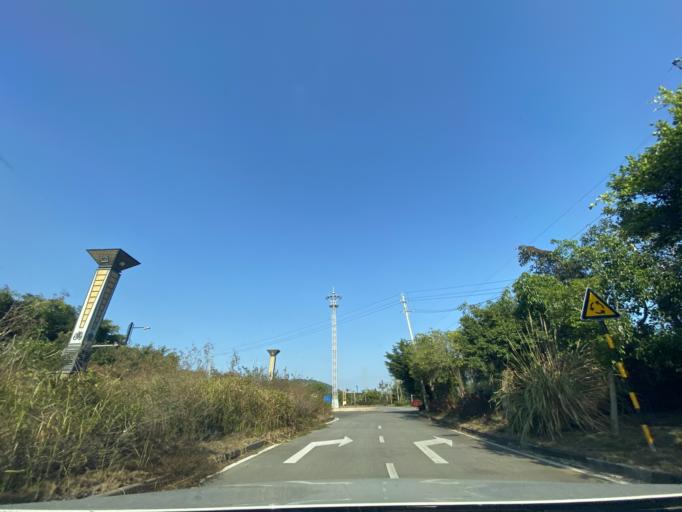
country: CN
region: Hainan
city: Yingzhou
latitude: 18.4500
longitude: 109.8521
